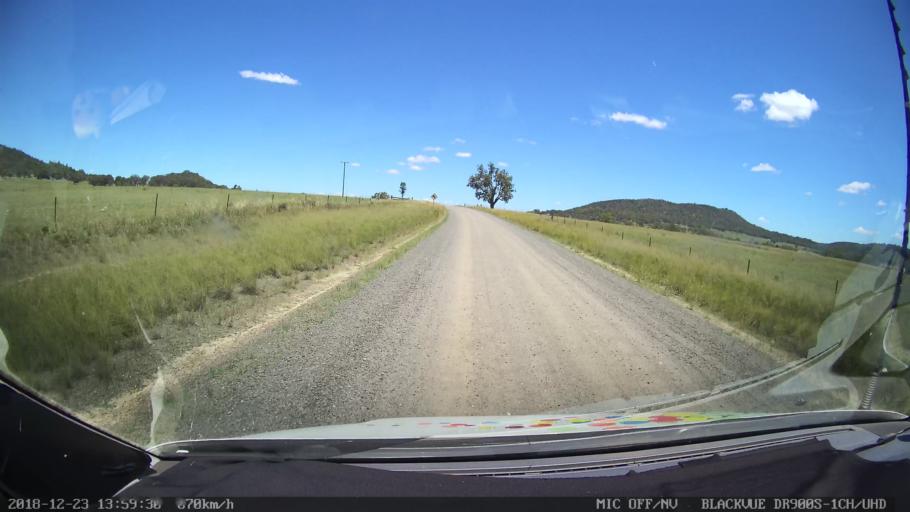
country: AU
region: New South Wales
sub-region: Tamworth Municipality
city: Manilla
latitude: -30.6087
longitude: 151.0963
